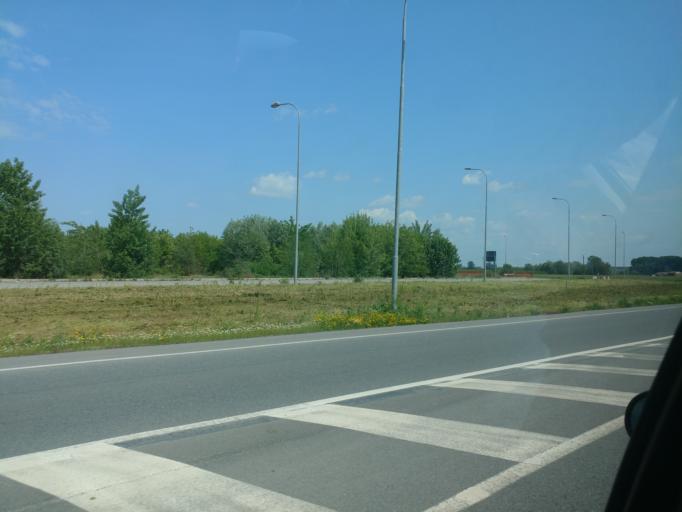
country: IT
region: Piedmont
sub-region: Provincia di Cuneo
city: Carde
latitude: 44.7341
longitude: 7.4221
